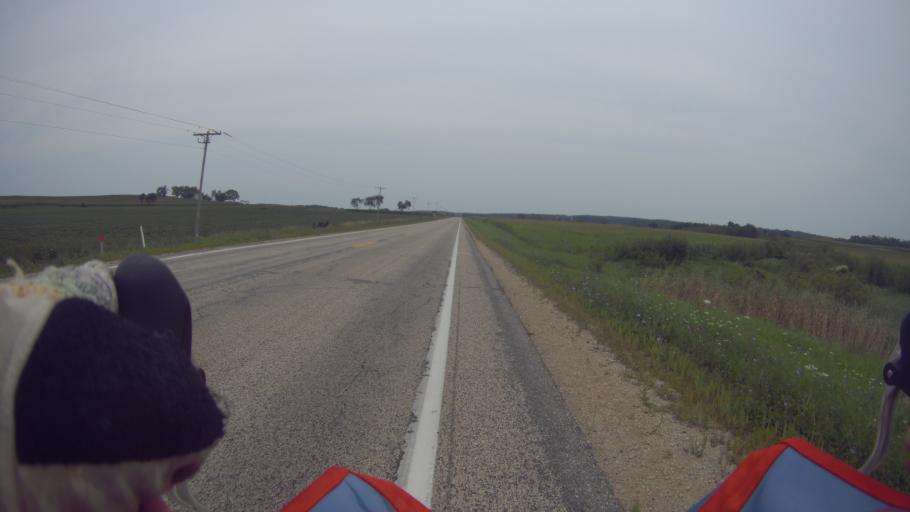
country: US
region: Wisconsin
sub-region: Green County
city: New Glarus
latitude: 42.9029
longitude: -89.6219
